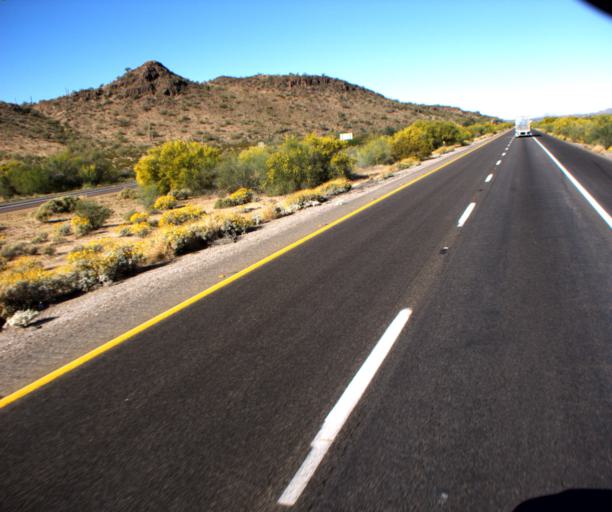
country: US
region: Arizona
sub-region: Pinal County
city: Maricopa
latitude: 32.8356
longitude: -112.1809
